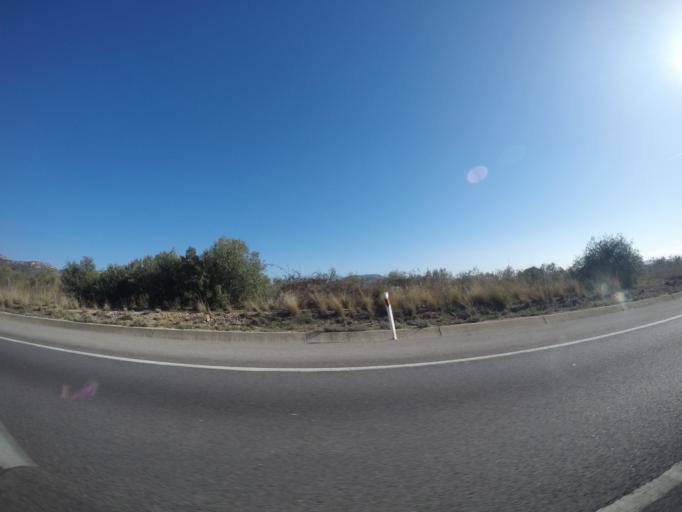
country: ES
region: Catalonia
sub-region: Provincia de Barcelona
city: Esparreguera
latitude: 41.5461
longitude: 1.8531
